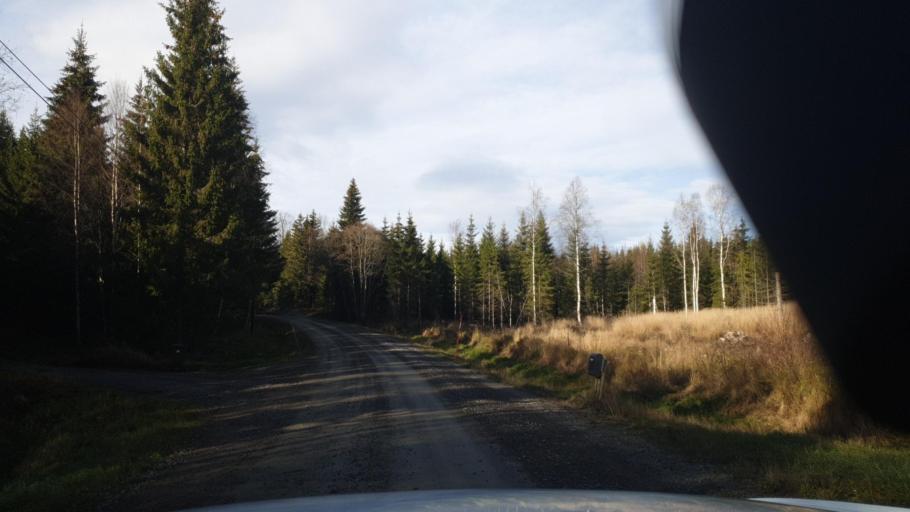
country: SE
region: Vaermland
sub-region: Eda Kommun
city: Charlottenberg
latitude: 59.9703
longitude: 12.5021
